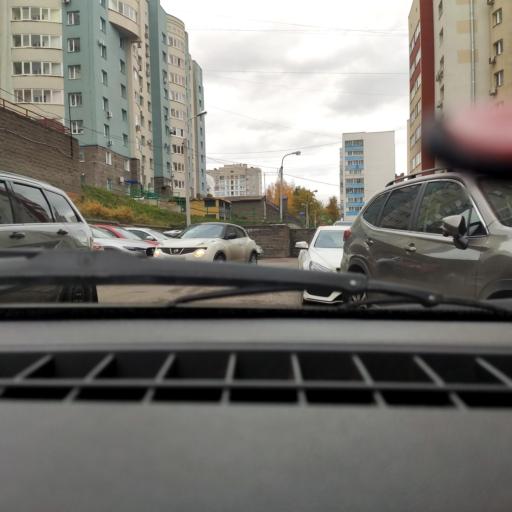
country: RU
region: Bashkortostan
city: Ufa
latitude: 54.7462
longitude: 55.9539
